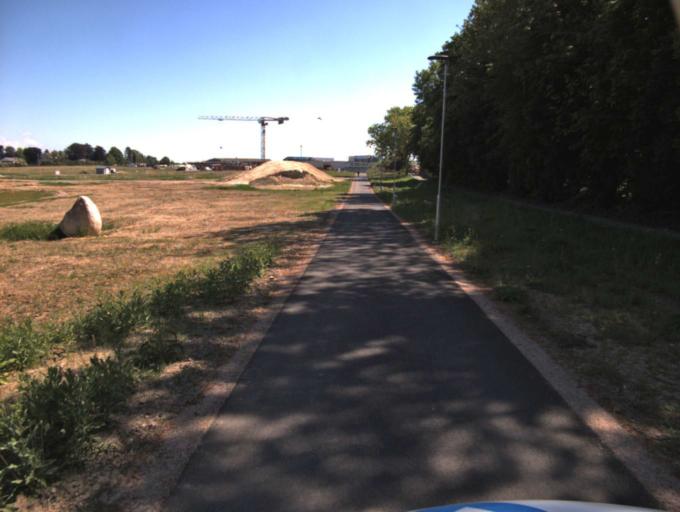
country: SE
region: Skane
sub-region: Kristianstads Kommun
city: Kristianstad
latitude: 56.0268
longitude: 14.1978
